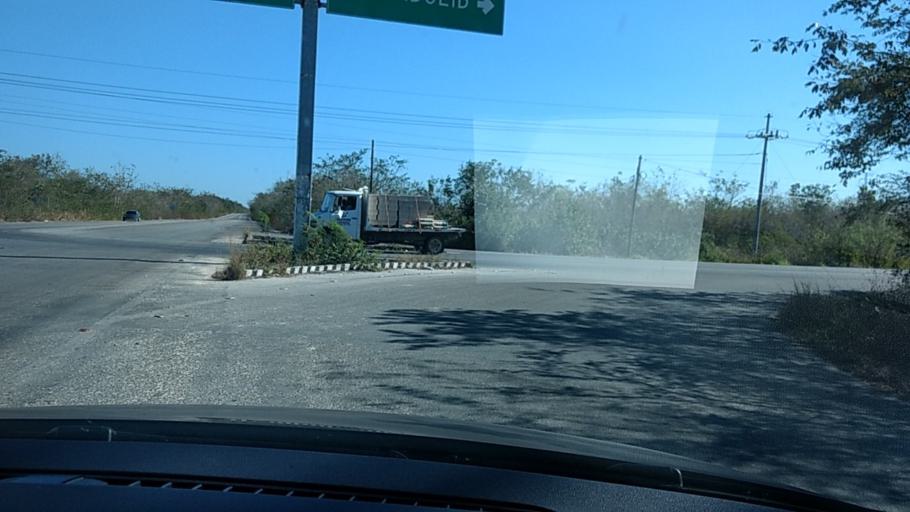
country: MX
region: Yucatan
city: Valladolid
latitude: 20.7026
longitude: -88.2410
